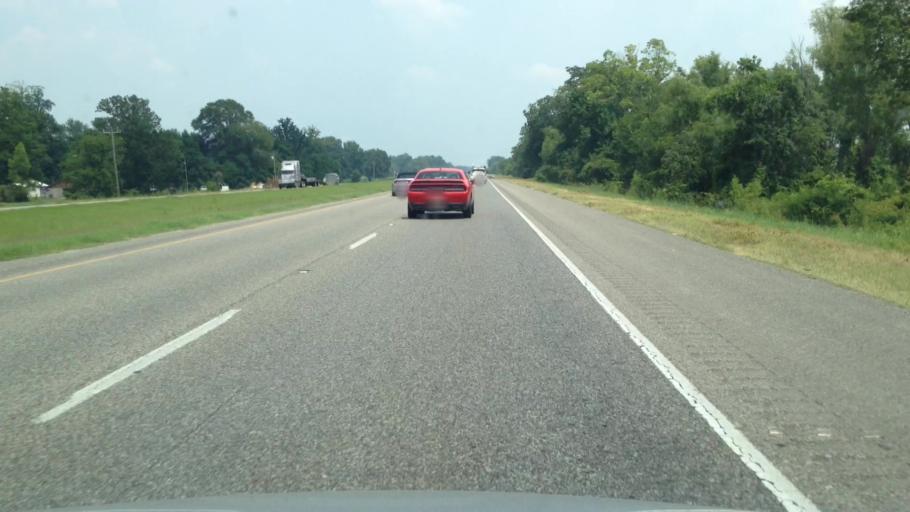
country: US
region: Louisiana
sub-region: West Baton Rouge Parish
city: Erwinville
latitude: 30.5169
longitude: -91.3597
